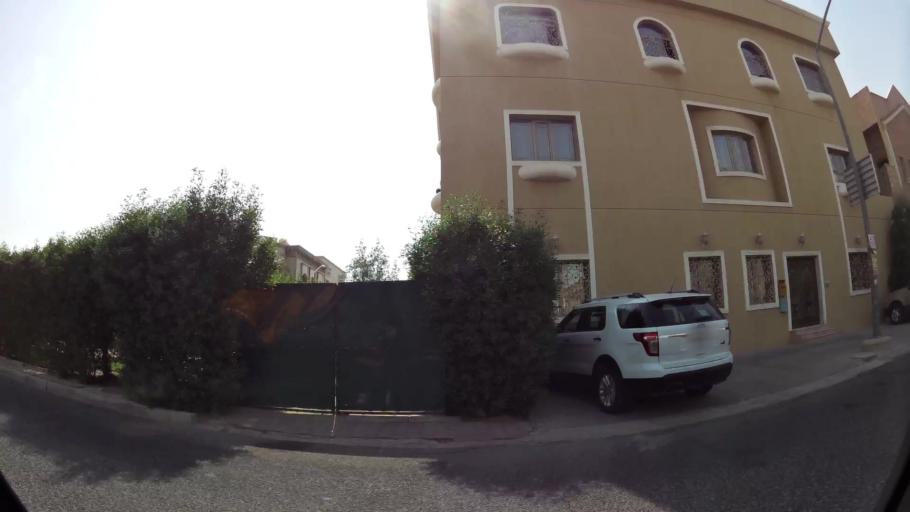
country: KW
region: Muhafazat al Jahra'
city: Al Jahra'
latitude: 29.3028
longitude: 47.7110
